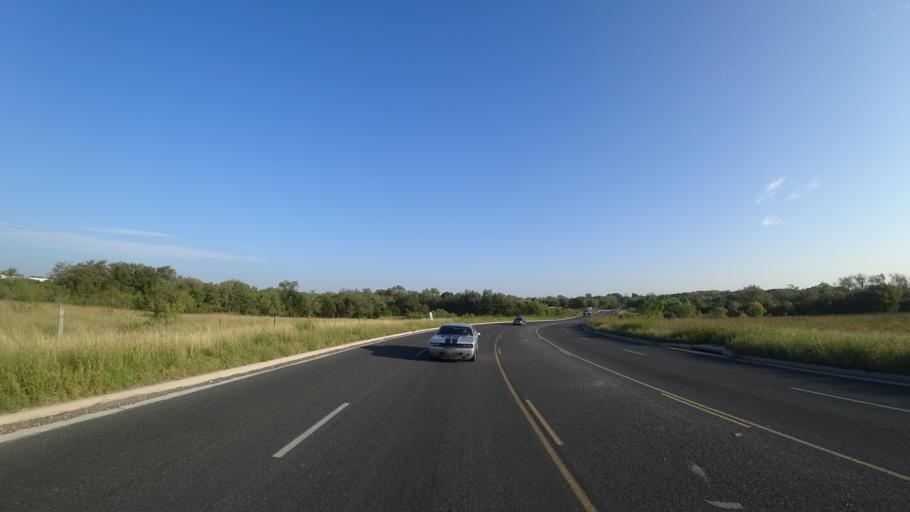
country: US
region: Texas
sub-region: Travis County
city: Austin
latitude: 30.3397
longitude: -97.6643
